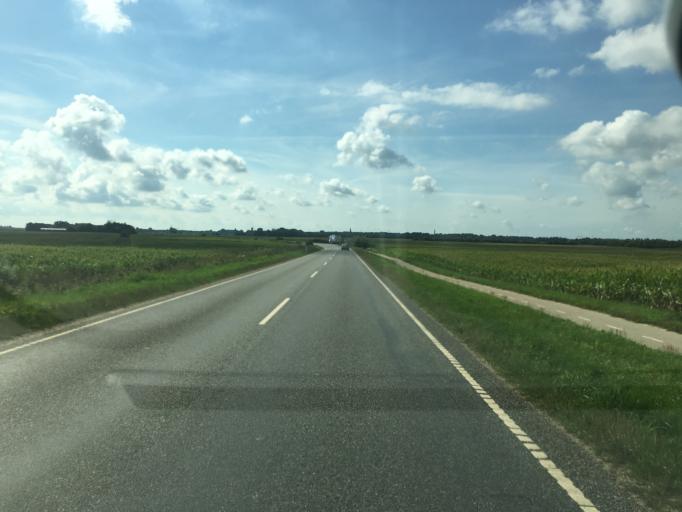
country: DK
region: South Denmark
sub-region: Tonder Kommune
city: Tonder
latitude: 54.9335
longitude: 8.9131
